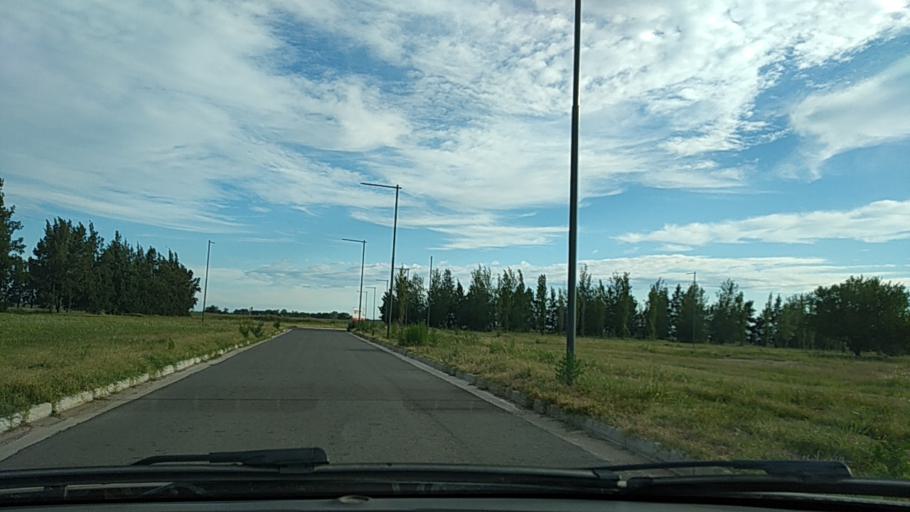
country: AR
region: Santa Fe
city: Funes
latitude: -32.9463
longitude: -60.7683
